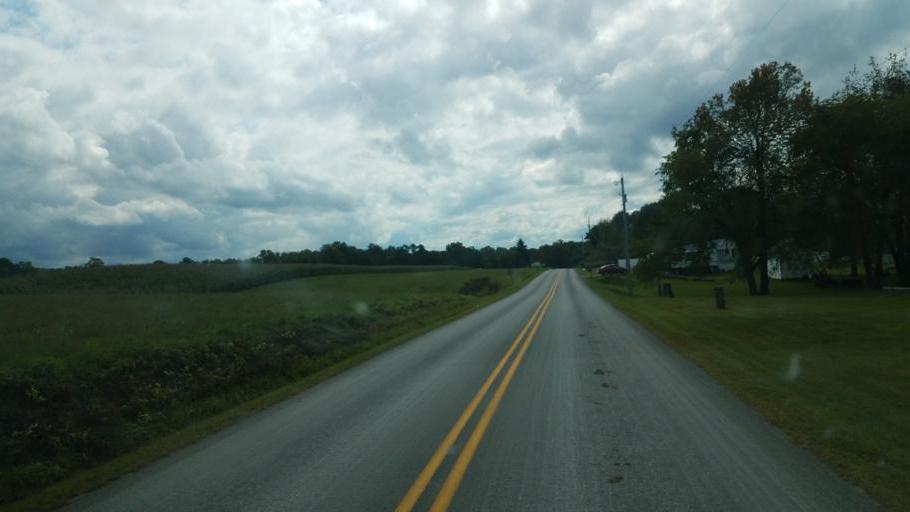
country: US
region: Pennsylvania
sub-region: Mercer County
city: Greenville
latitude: 41.4889
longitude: -80.3385
